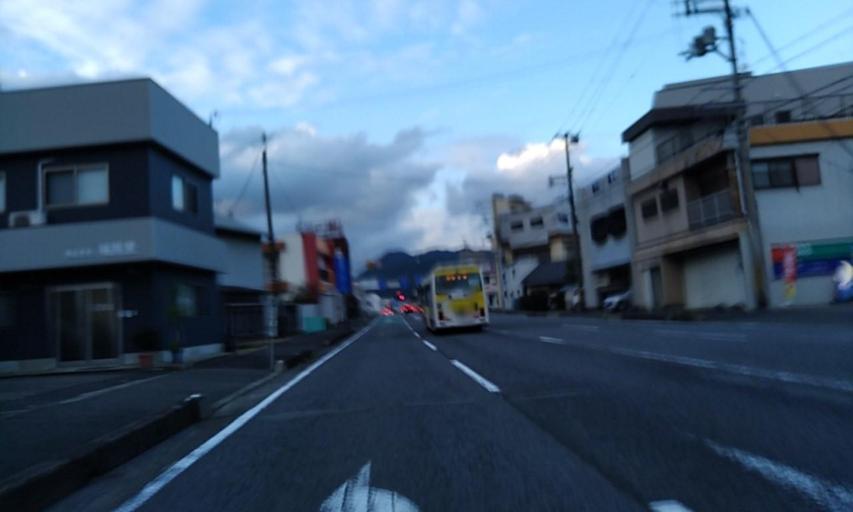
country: JP
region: Wakayama
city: Shingu
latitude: 33.7176
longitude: 135.9872
